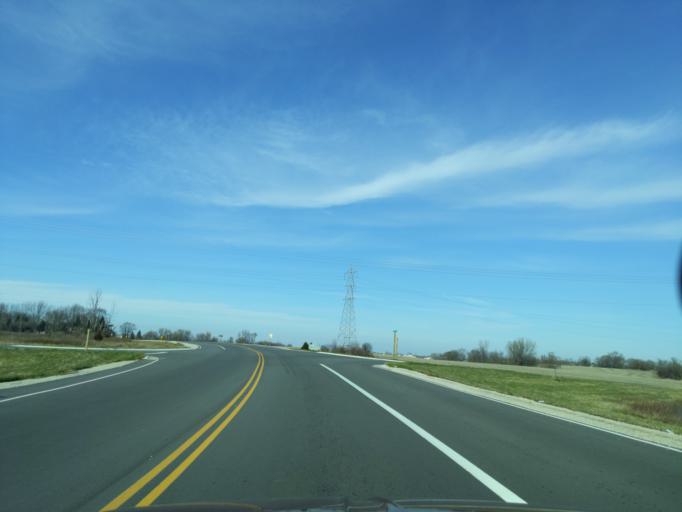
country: US
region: Wisconsin
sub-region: Walworth County
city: Whitewater
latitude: 42.8215
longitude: -88.7004
